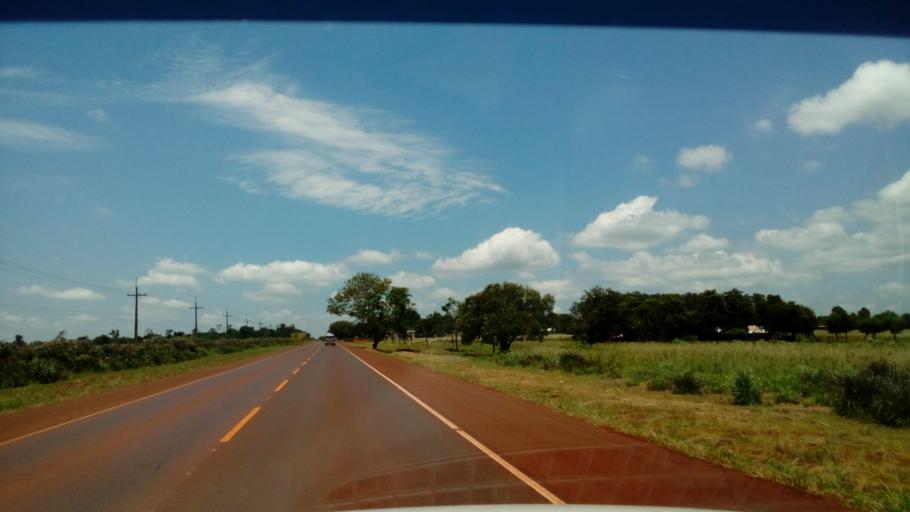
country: PY
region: Alto Parana
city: Naranjal
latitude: -25.9811
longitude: -55.1165
